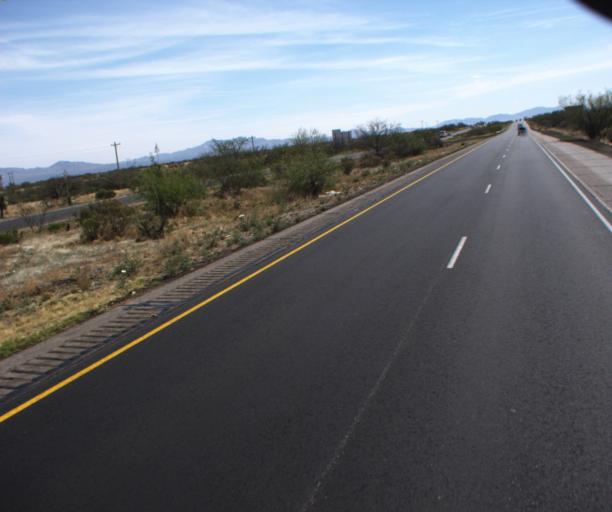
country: US
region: Arizona
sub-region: Cochise County
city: Mescal
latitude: 31.9628
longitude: -110.4227
